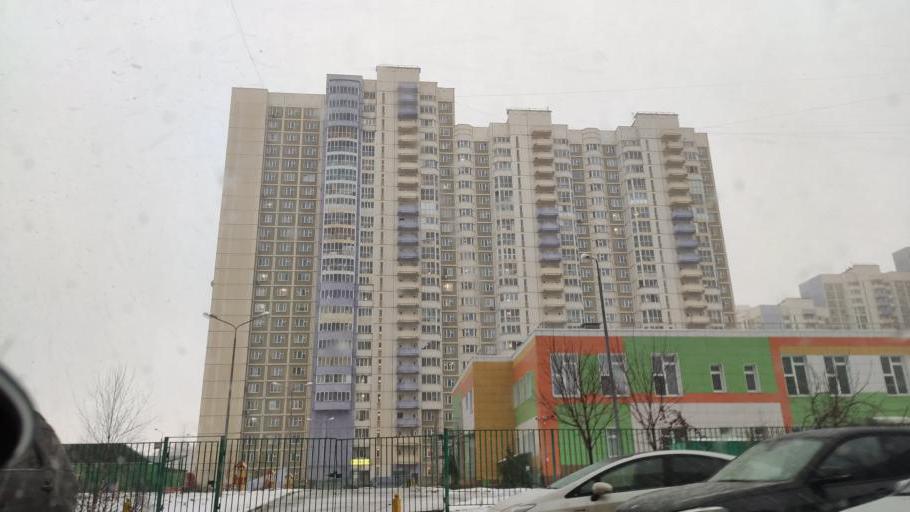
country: RU
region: Moscow
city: Khimki
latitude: 55.9064
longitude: 37.3932
